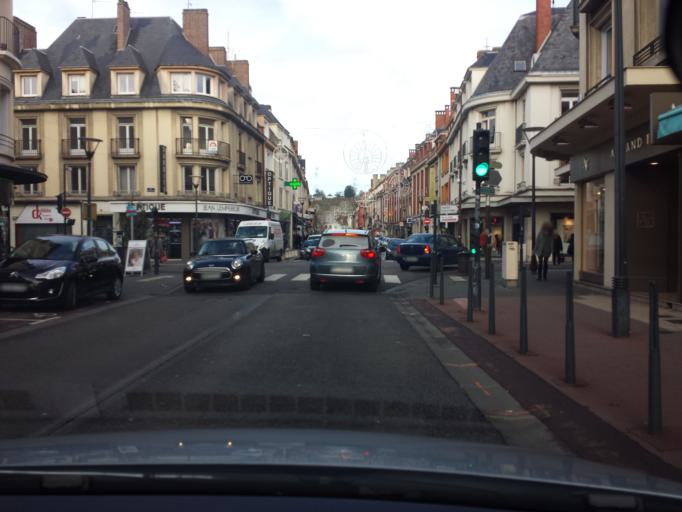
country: FR
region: Haute-Normandie
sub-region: Departement de l'Eure
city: Evreux
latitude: 49.0239
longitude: 1.1490
